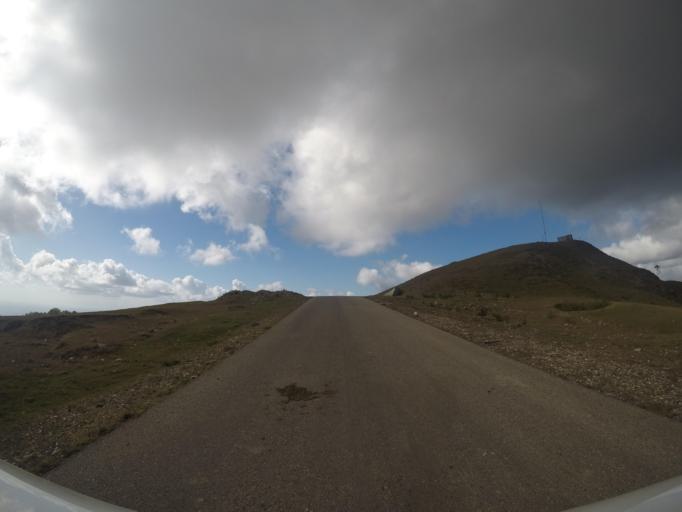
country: TL
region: Lautem
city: Lospalos
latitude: -8.4757
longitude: 126.8689
